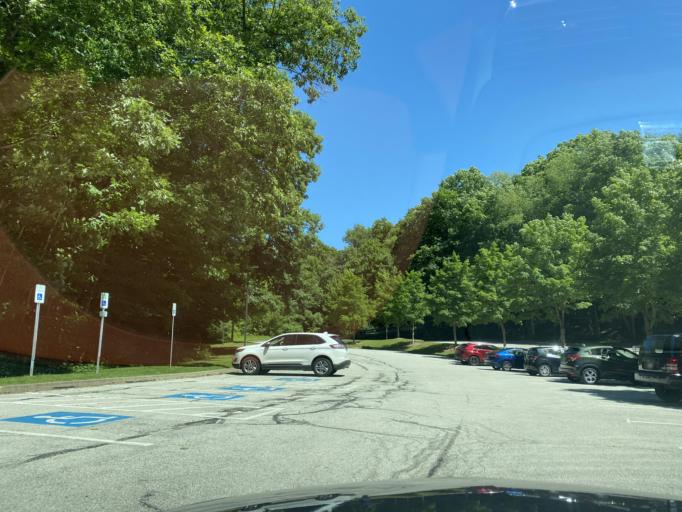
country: US
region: Ohio
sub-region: Summit County
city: Akron
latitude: 41.1274
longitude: -81.5403
